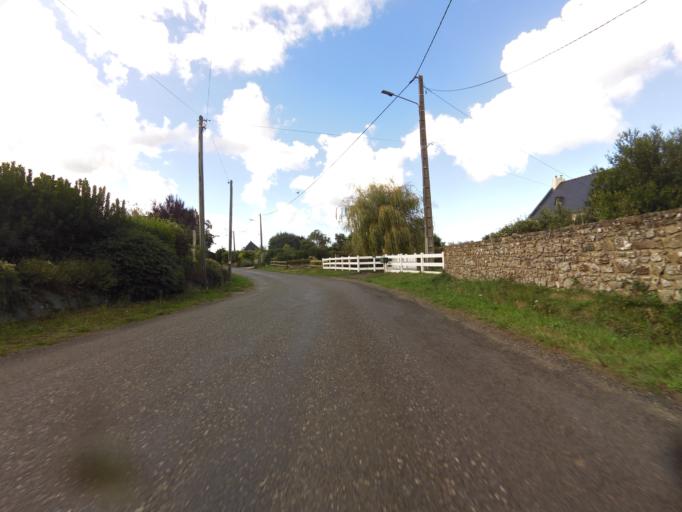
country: FR
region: Brittany
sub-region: Departement des Cotes-d'Armor
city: Plouha
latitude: 48.6688
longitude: -2.8878
